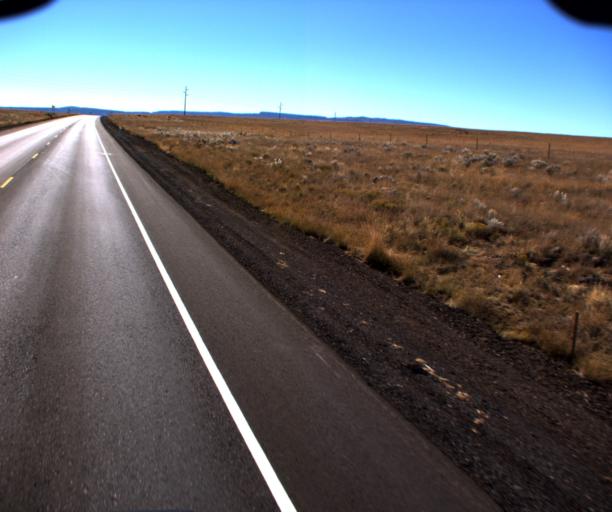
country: US
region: Arizona
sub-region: Apache County
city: Springerville
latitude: 34.1865
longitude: -109.3199
